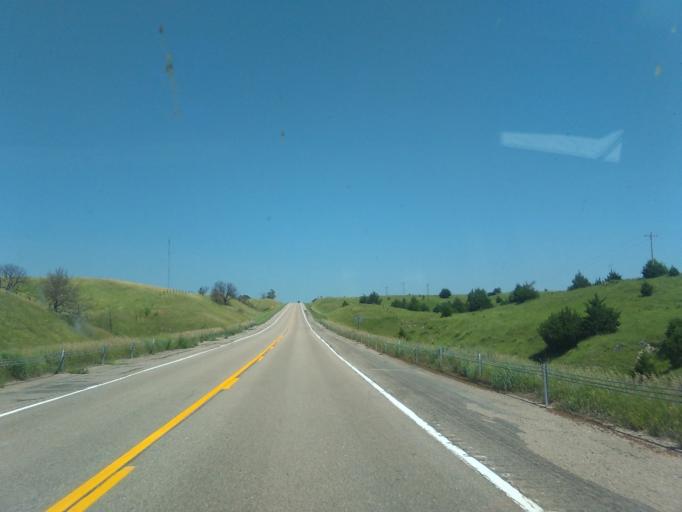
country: US
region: Nebraska
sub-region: Frontier County
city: Stockville
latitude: 40.5920
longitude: -100.6295
